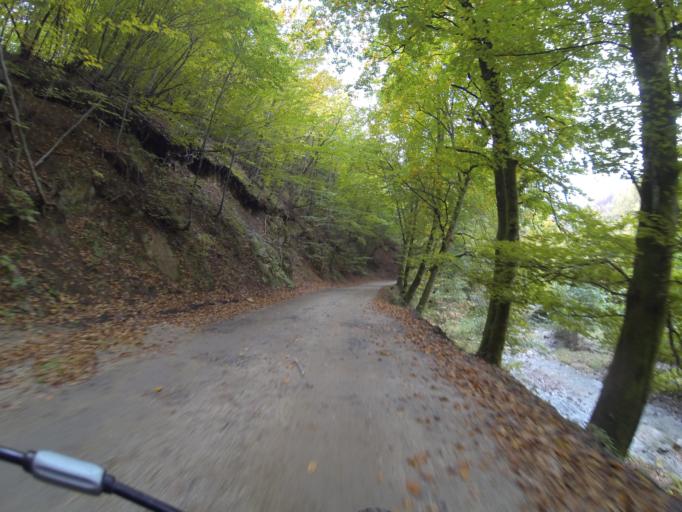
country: RO
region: Gorj
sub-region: Comuna Tismana
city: Sohodol
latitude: 45.0622
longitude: 22.8968
